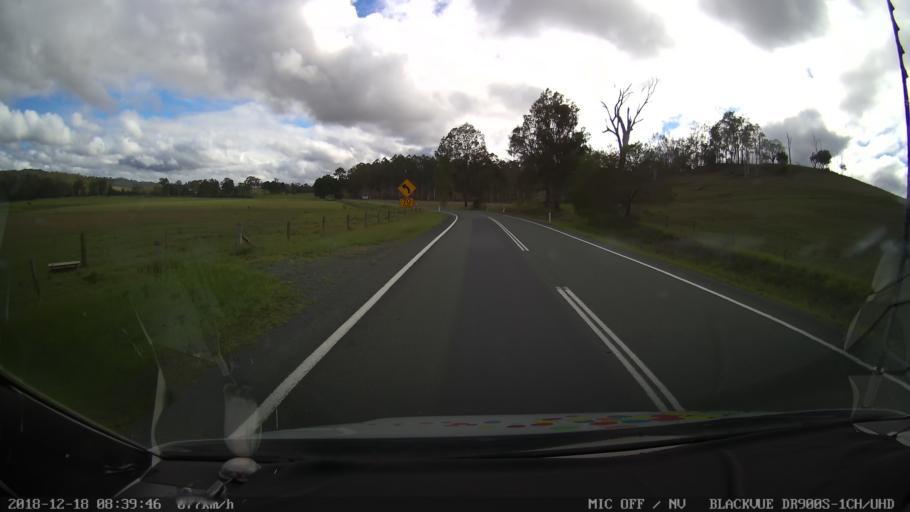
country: AU
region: Queensland
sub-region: Logan
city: Cedar Vale
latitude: -28.2484
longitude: 152.8417
